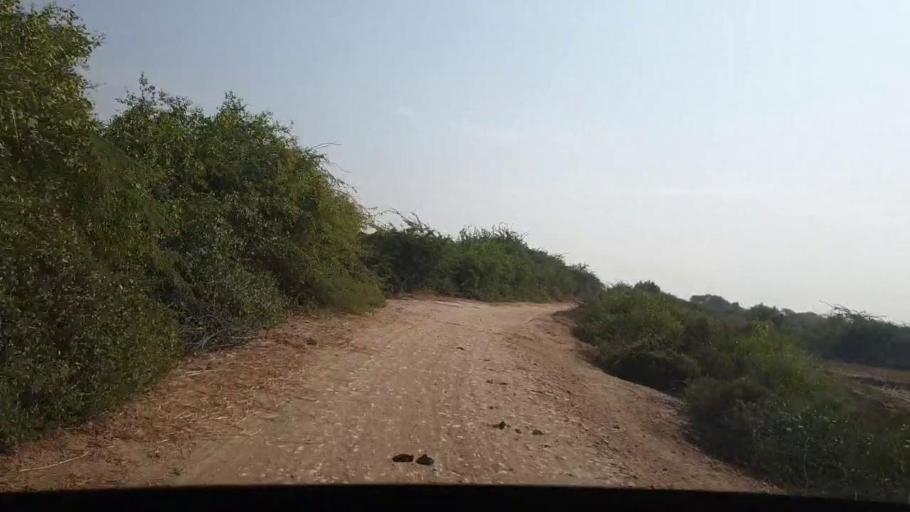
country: PK
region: Sindh
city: Chuhar Jamali
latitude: 24.2689
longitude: 67.9233
